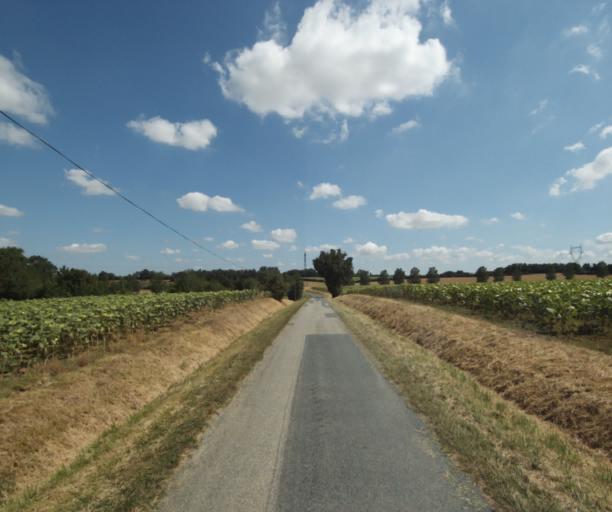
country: FR
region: Midi-Pyrenees
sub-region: Departement de la Haute-Garonne
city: Auriac-sur-Vendinelle
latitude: 43.4687
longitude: 1.8004
